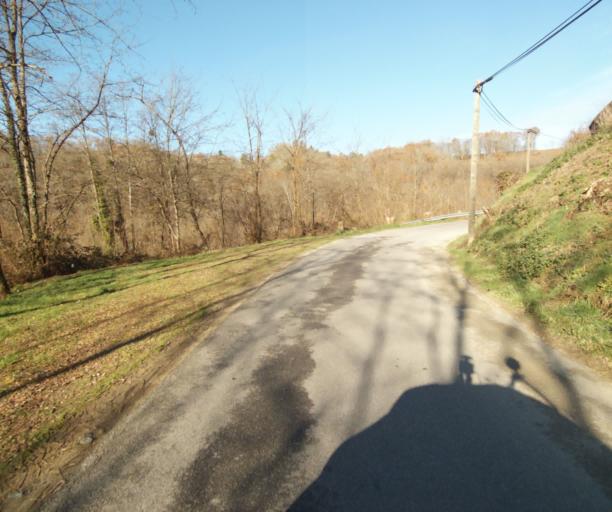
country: FR
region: Limousin
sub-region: Departement de la Correze
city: Chameyrat
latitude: 45.2358
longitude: 1.7313
